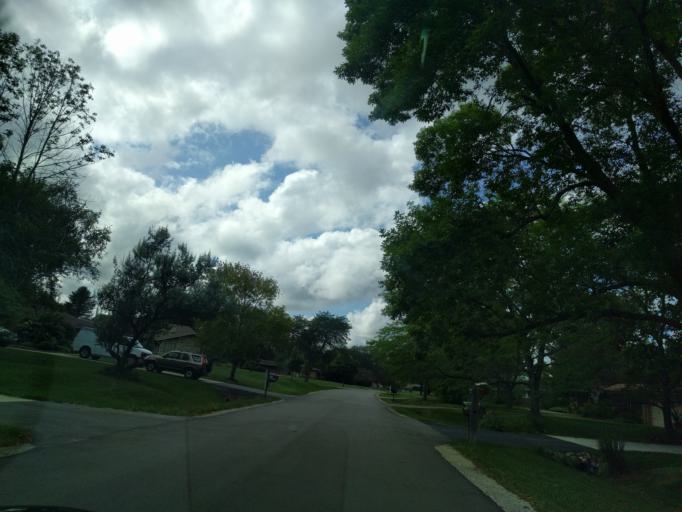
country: US
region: Wisconsin
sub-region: Milwaukee County
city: Bayside
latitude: 43.1857
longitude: -87.8972
